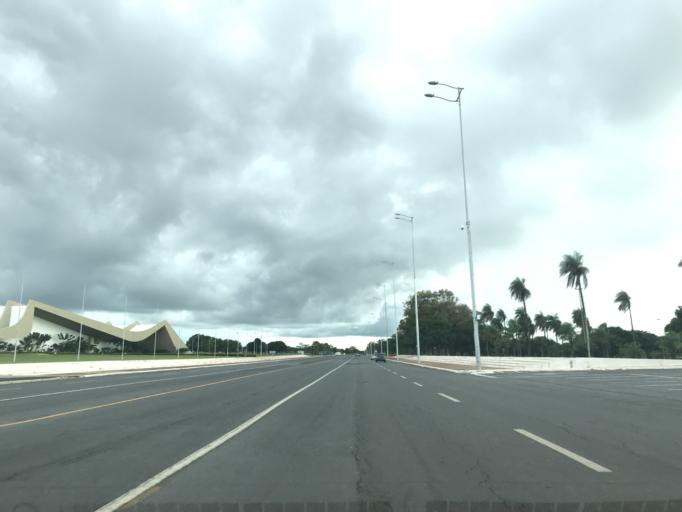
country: BR
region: Federal District
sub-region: Brasilia
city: Brasilia
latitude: -15.7731
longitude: -47.9200
